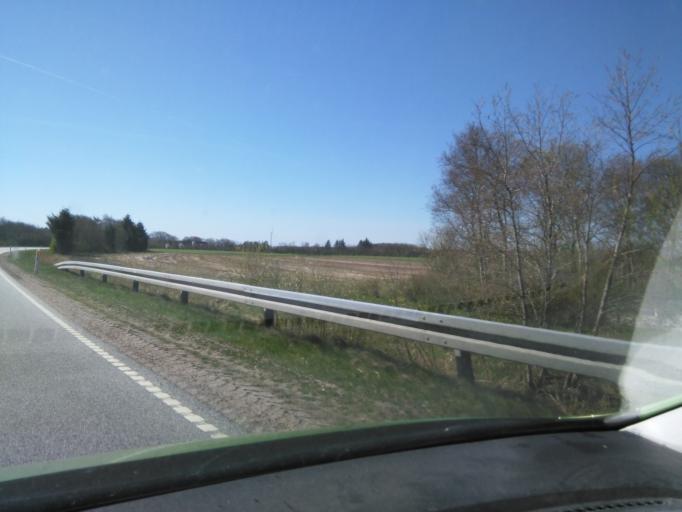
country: DK
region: South Denmark
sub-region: Varde Kommune
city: Varde
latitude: 55.6588
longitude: 8.5594
